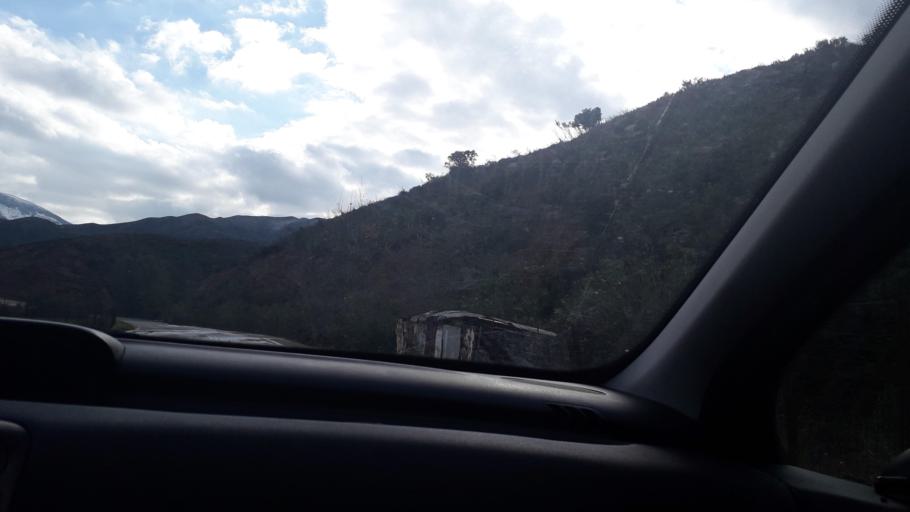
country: GR
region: Crete
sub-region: Nomos Rethymnis
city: Agia Foteini
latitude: 35.2838
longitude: 24.5620
